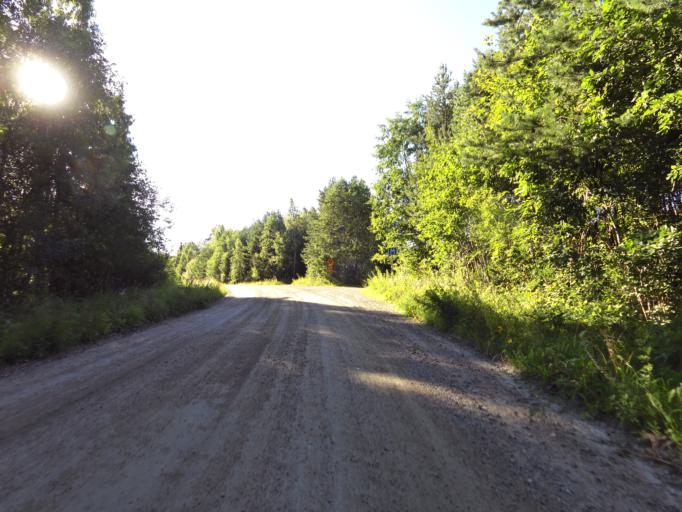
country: SE
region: Gaevleborg
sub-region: Hofors Kommun
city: Hofors
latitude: 60.5678
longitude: 16.2770
